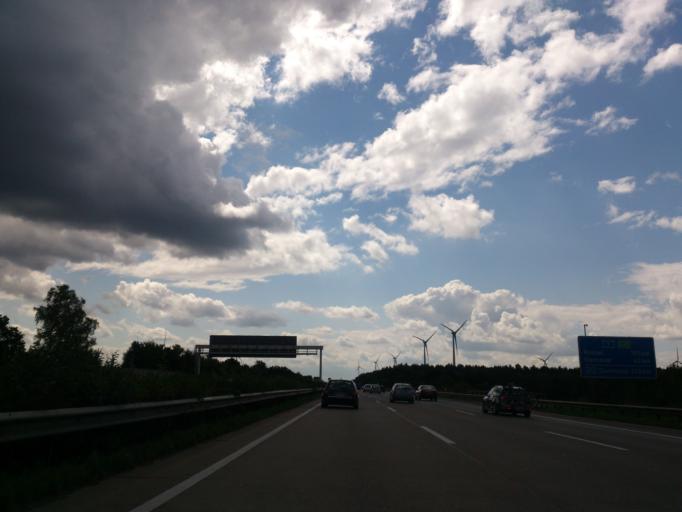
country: DE
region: Lower Saxony
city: Essel
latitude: 52.6701
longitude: 9.6949
